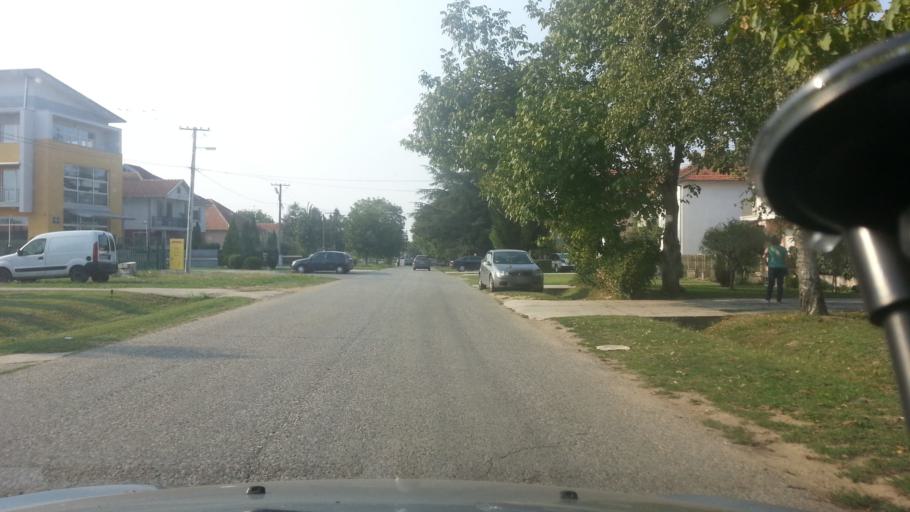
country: RS
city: Novi Banovci
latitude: 44.9480
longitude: 20.2863
